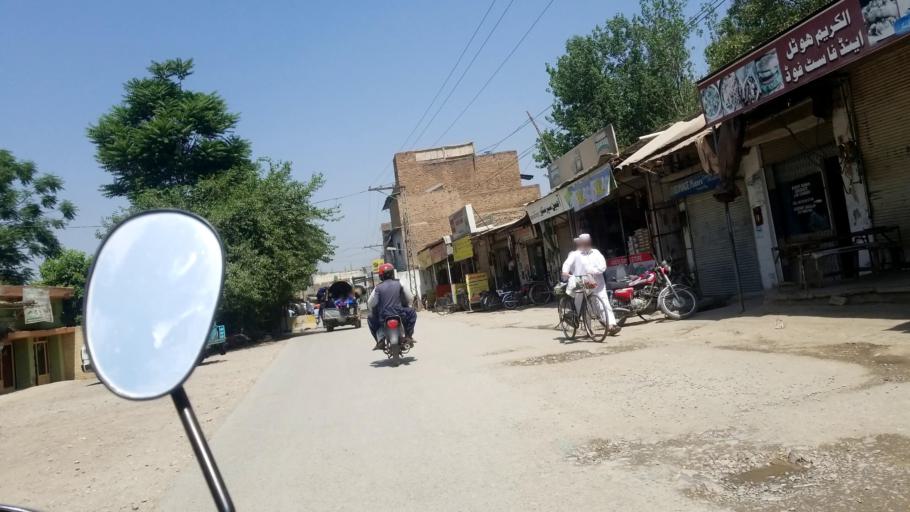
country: PK
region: Khyber Pakhtunkhwa
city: Peshawar
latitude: 34.0222
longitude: 71.4850
